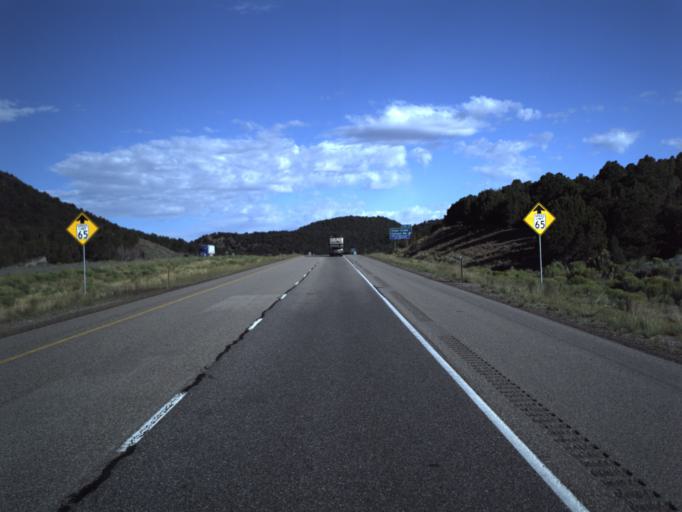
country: US
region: Utah
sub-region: Beaver County
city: Beaver
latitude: 38.5830
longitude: -112.4847
